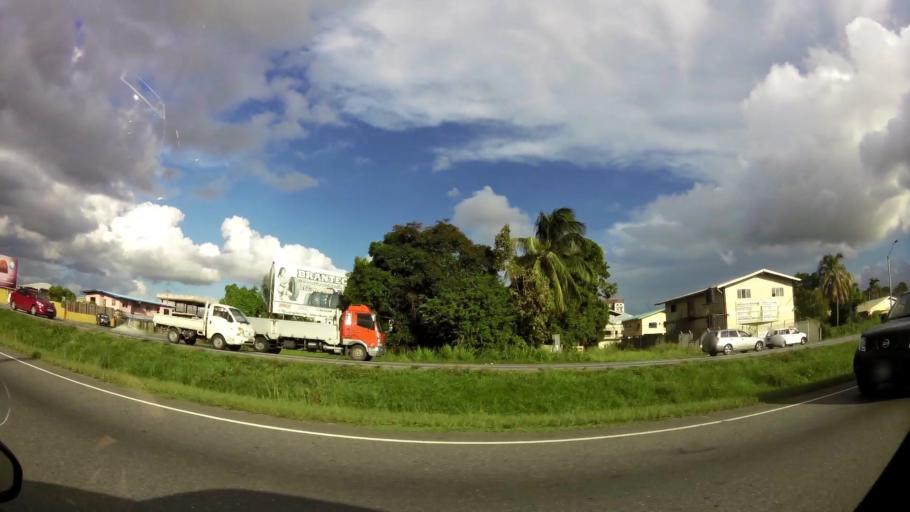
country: TT
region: Chaguanas
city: Chaguanas
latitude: 10.5127
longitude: -61.4077
